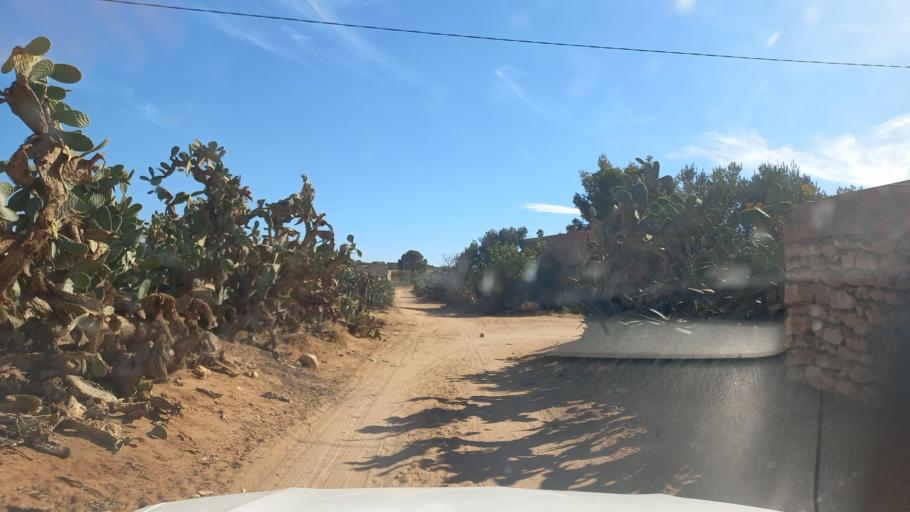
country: TN
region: Al Qasrayn
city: Kasserine
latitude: 35.2096
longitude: 8.9721
